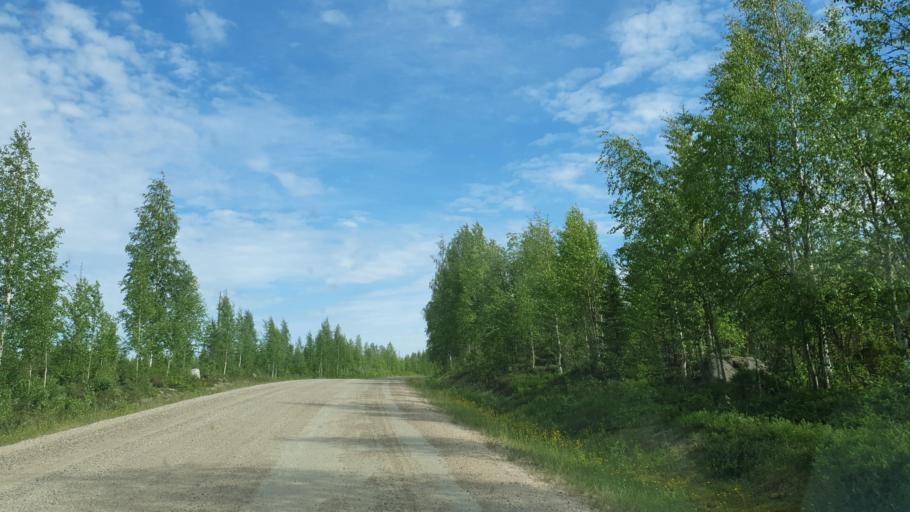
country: FI
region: Kainuu
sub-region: Kehys-Kainuu
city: Kuhmo
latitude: 64.4883
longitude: 29.5141
